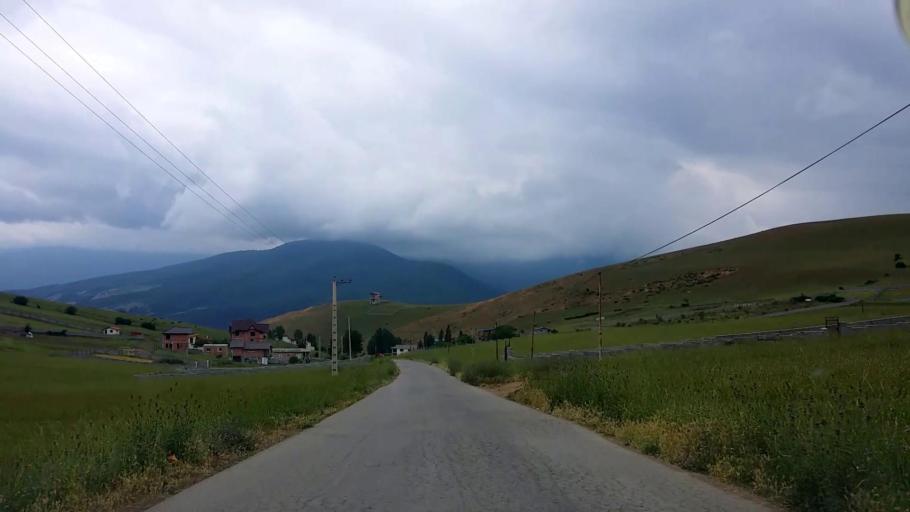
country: IR
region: Mazandaran
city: Chalus
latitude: 36.5247
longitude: 51.2638
